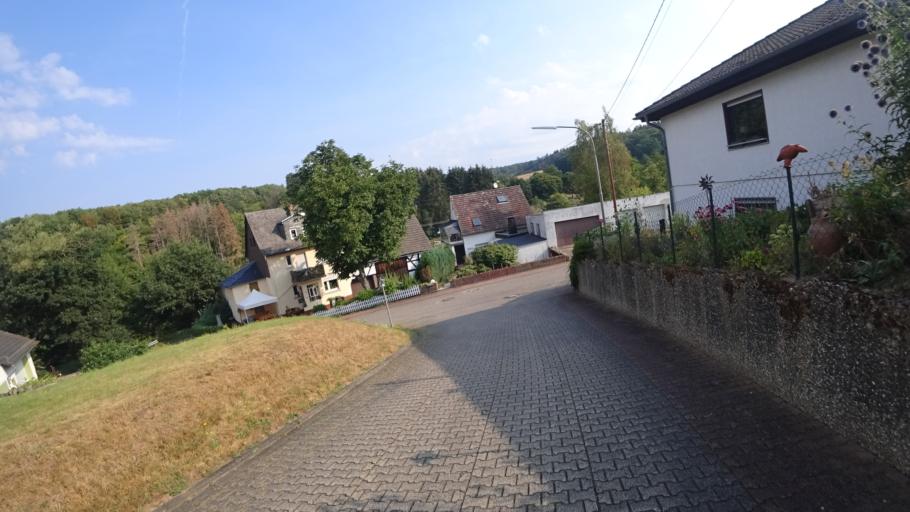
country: DE
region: Rheinland-Pfalz
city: Hundsdorf
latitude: 50.4712
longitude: 7.7034
